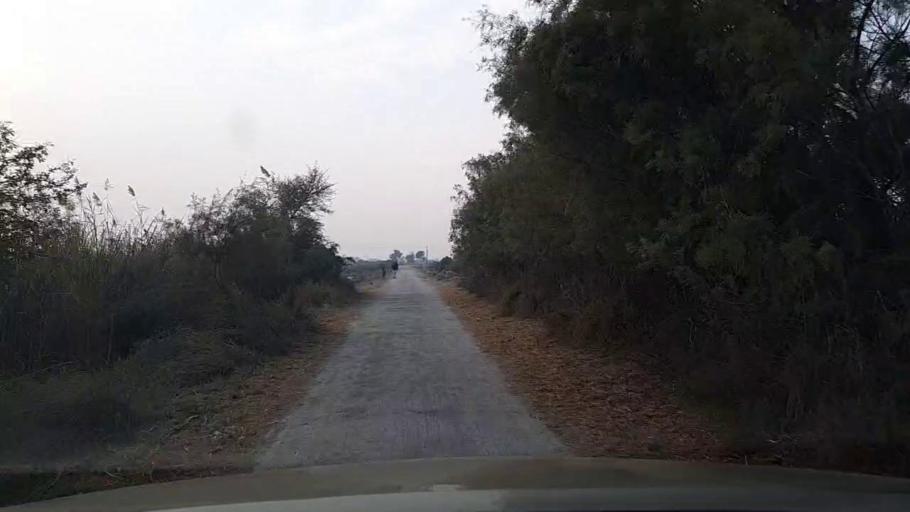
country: PK
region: Sindh
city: Sanghar
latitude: 26.1857
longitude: 68.9572
